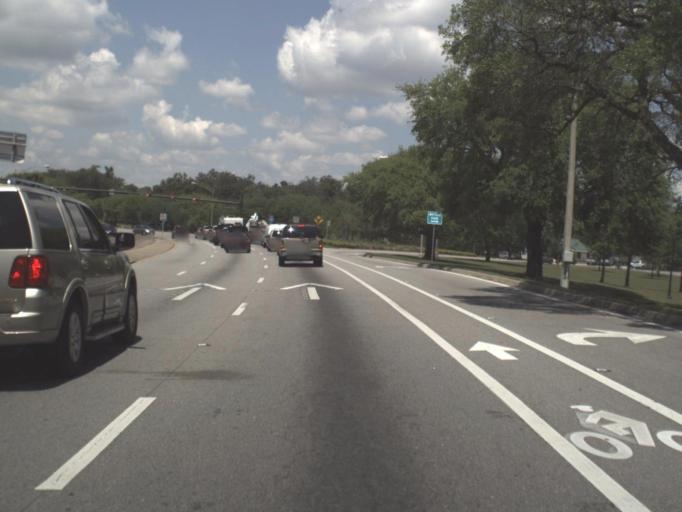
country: US
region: Florida
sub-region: Escambia County
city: East Pensacola Heights
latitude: 30.4171
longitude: -87.1936
